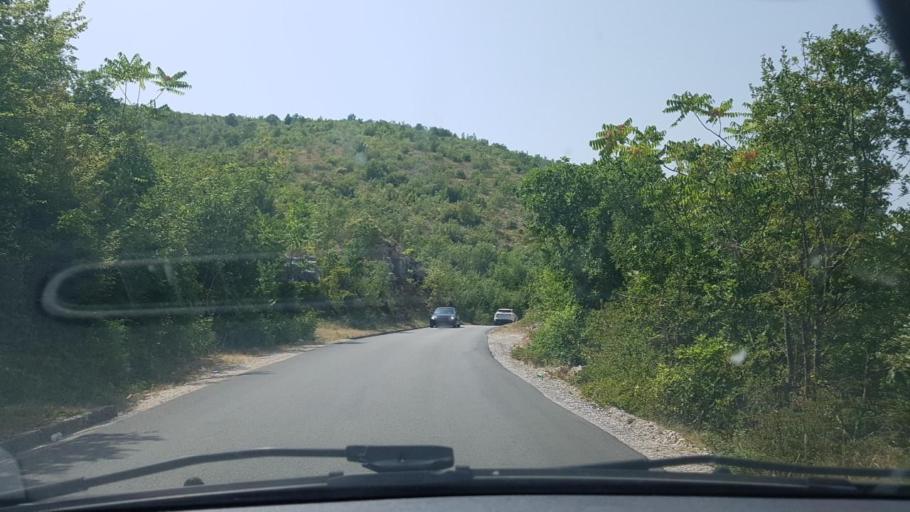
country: HR
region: Dubrovacko-Neretvanska
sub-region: Grad Dubrovnik
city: Metkovic
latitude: 43.0391
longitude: 17.7137
